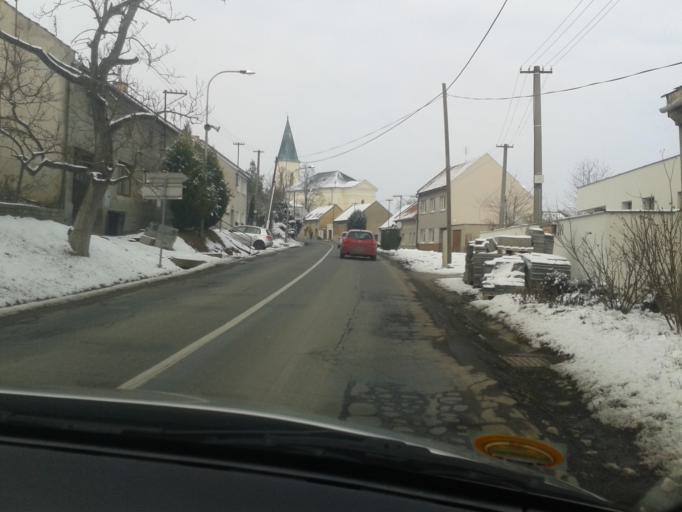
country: CZ
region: Olomoucky
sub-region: Okres Prostejov
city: Plumlov
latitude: 49.4871
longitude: 17.0189
